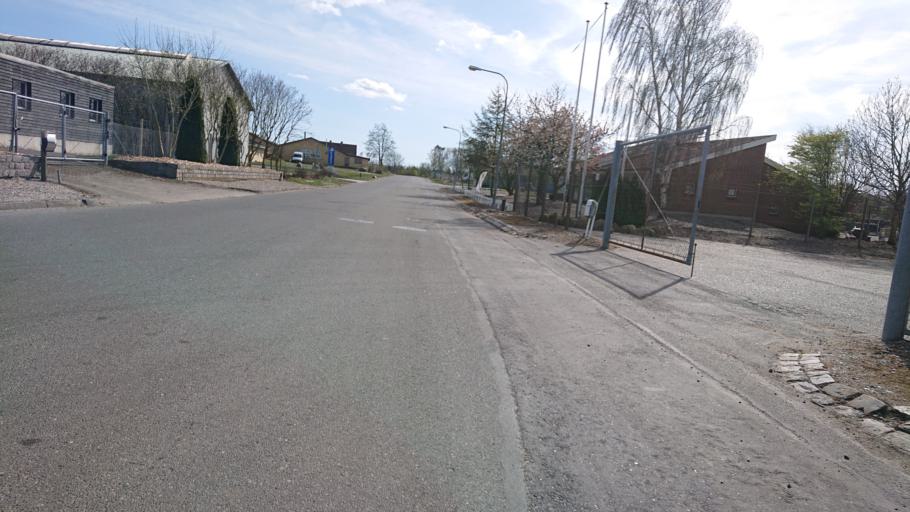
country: DK
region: South Denmark
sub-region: Nyborg Kommune
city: Nyborg
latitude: 55.3124
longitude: 10.7520
